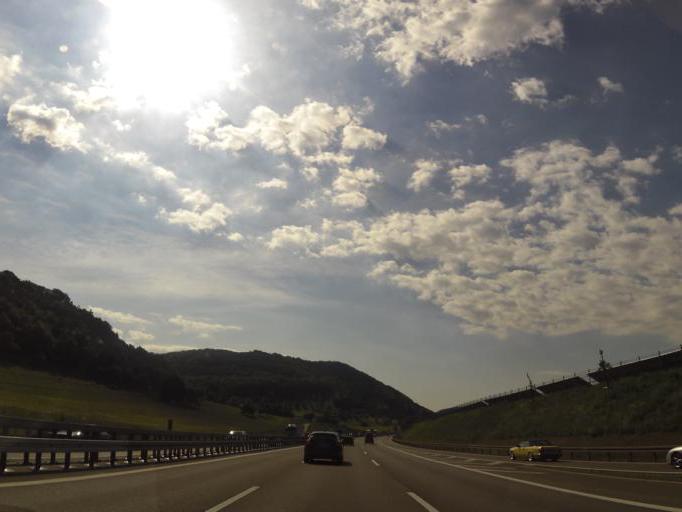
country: DE
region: Baden-Wuerttemberg
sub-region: Regierungsbezirk Stuttgart
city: Gruibingen
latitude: 48.6054
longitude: 9.6357
